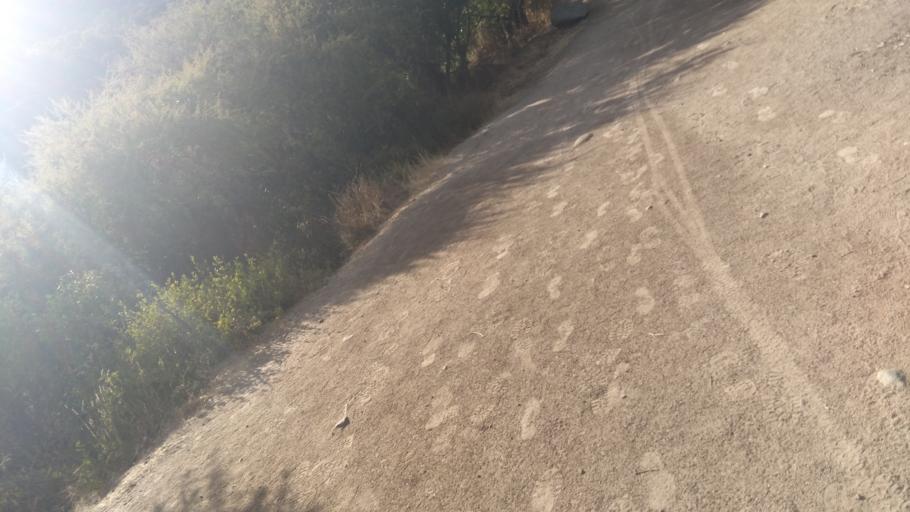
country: CL
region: Santiago Metropolitan
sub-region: Provincia de Cordillera
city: Puente Alto
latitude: -33.7257
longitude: -70.4840
